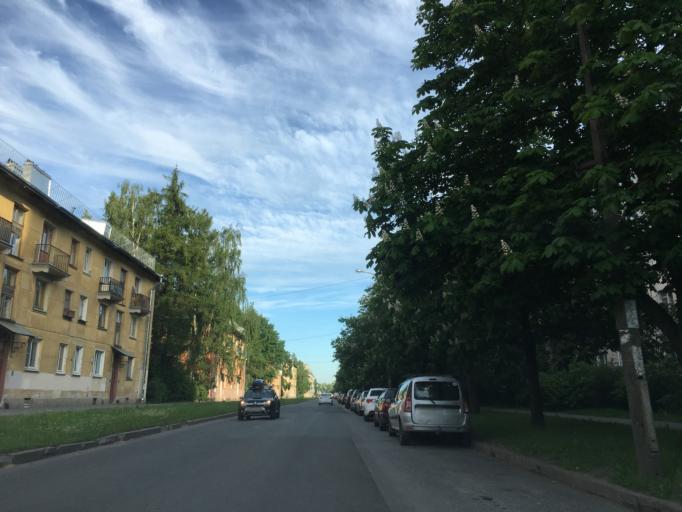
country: RU
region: St.-Petersburg
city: Dachnoye
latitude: 59.8375
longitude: 30.2518
